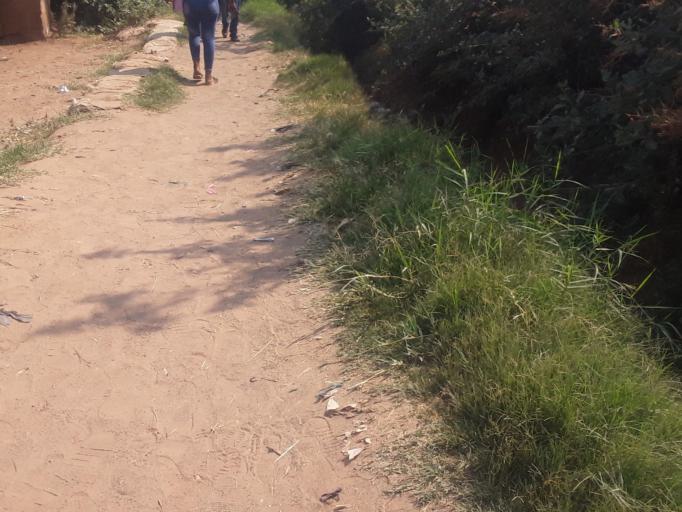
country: ZM
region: Lusaka
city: Lusaka
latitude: -15.3575
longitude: 28.2994
